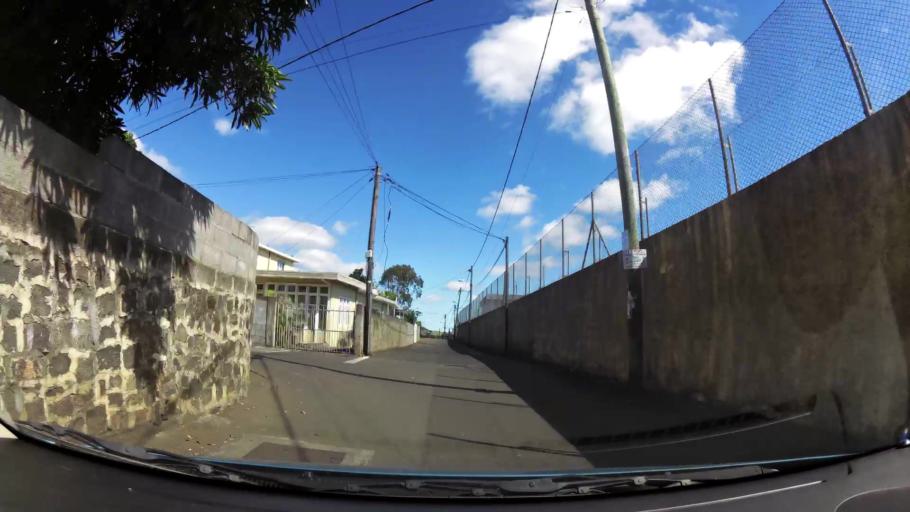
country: MU
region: Plaines Wilhems
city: Vacoas
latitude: -20.2917
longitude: 57.4773
